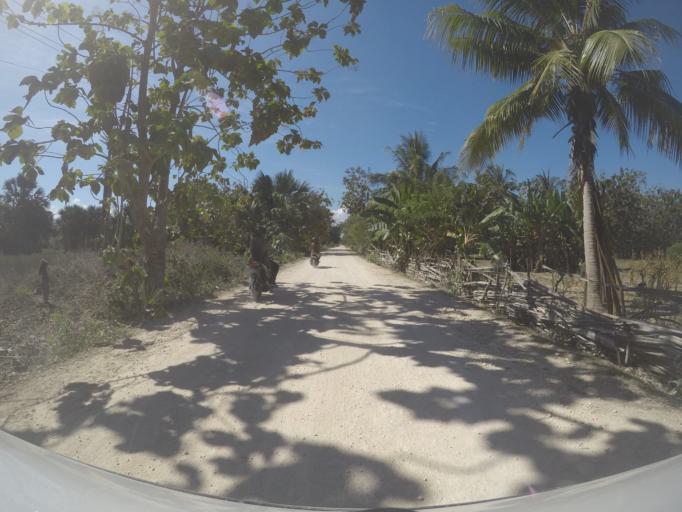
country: TL
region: Viqueque
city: Viqueque
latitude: -8.8945
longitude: 126.5065
